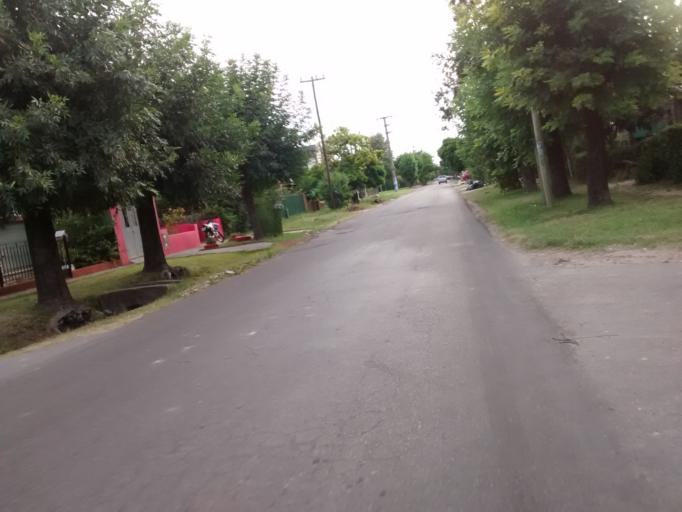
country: AR
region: Buenos Aires
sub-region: Partido de La Plata
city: La Plata
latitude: -34.8692
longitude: -58.0559
